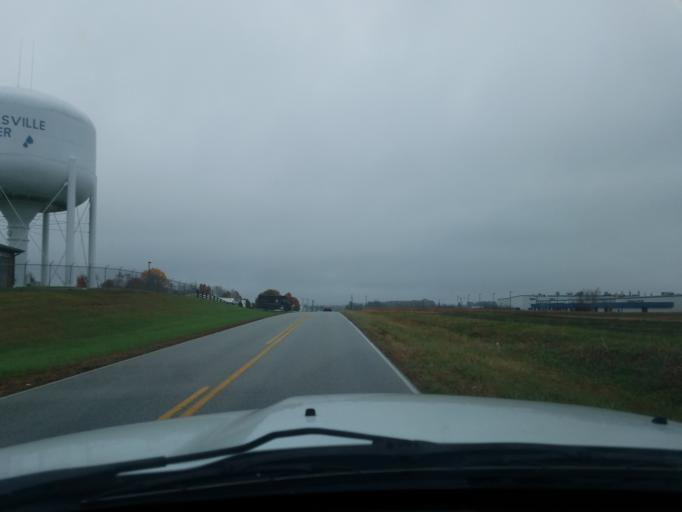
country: US
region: Kentucky
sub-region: Taylor County
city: Campbellsville
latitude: 37.3417
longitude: -85.3230
